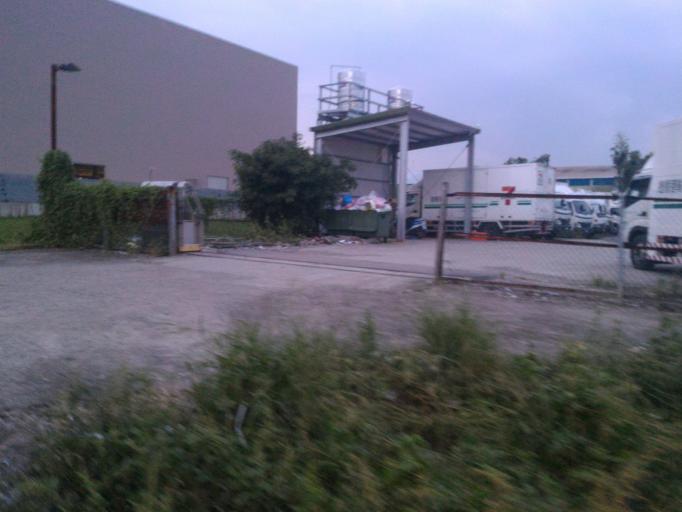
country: TW
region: Taiwan
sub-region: Taoyuan
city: Taoyuan
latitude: 24.9605
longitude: 121.3929
